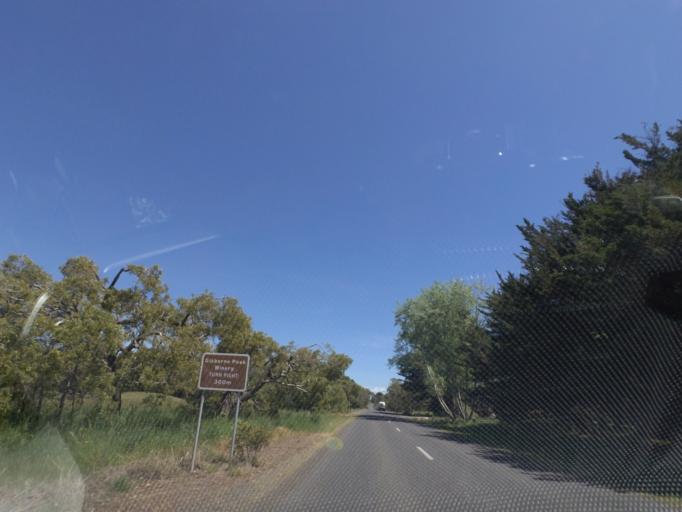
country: AU
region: Victoria
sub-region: Hume
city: Sunbury
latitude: -37.5400
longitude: 144.6078
